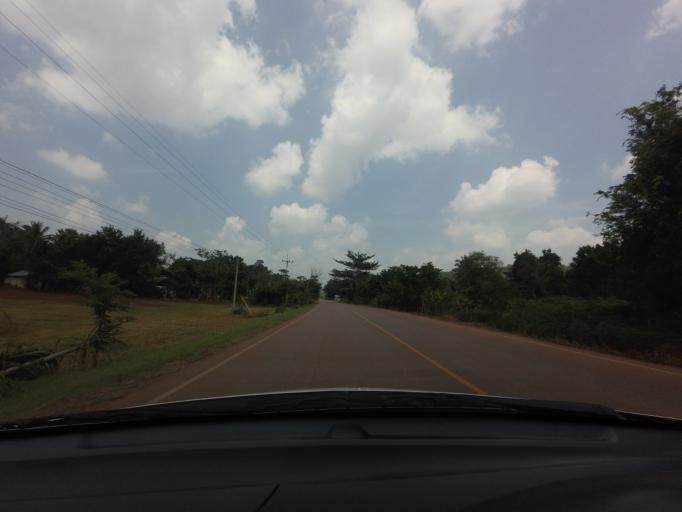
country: TH
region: Nakhon Ratchasima
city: Pak Chong
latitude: 14.5747
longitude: 101.5683
